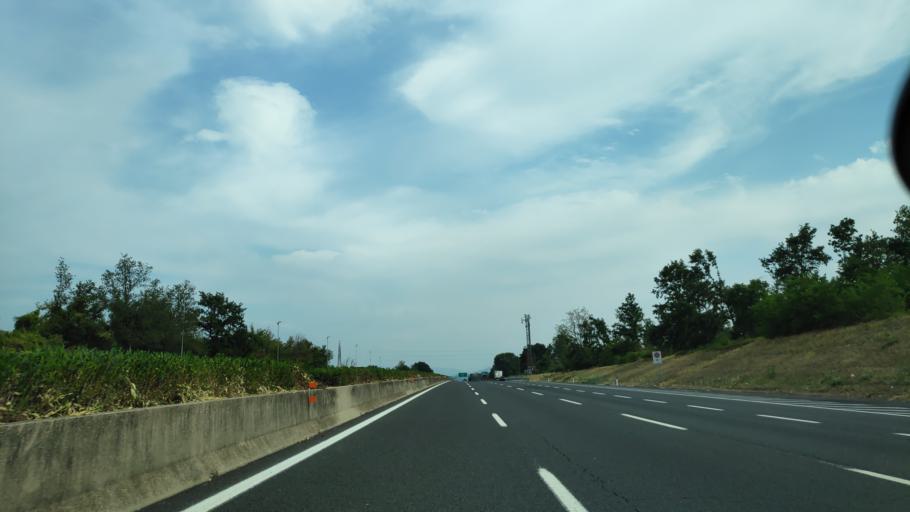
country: IT
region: Latium
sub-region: Citta metropolitana di Roma Capitale
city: Fiano Romano
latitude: 42.1720
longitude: 12.6095
